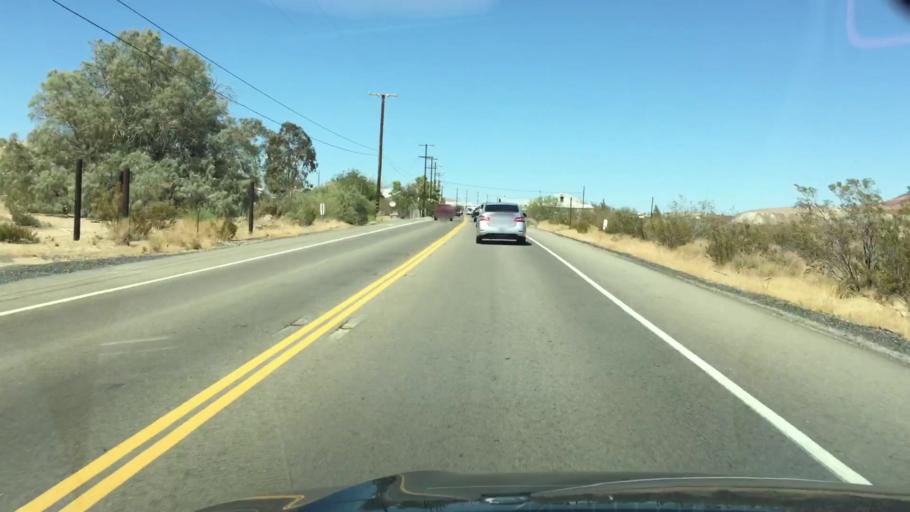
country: US
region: California
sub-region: Kern County
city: Ridgecrest
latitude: 35.3496
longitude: -117.6198
